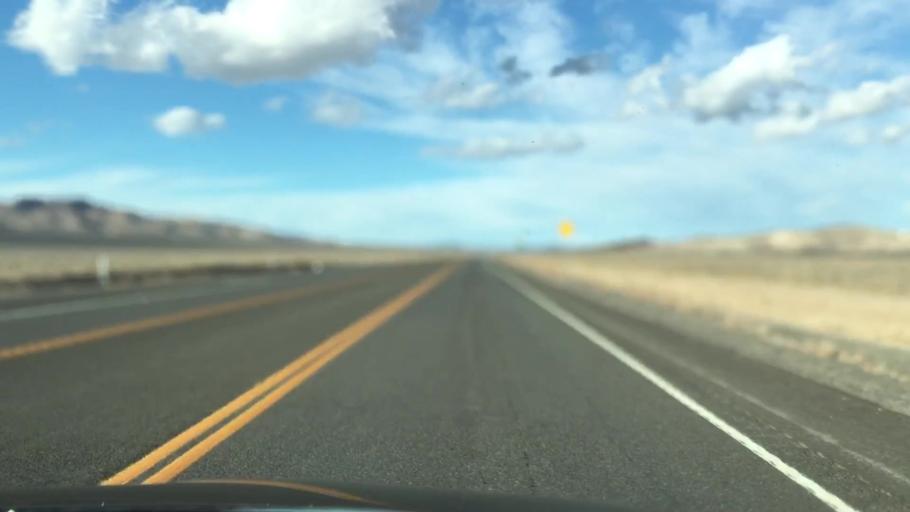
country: US
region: Nevada
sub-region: Esmeralda County
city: Goldfield
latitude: 37.5032
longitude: -117.1848
